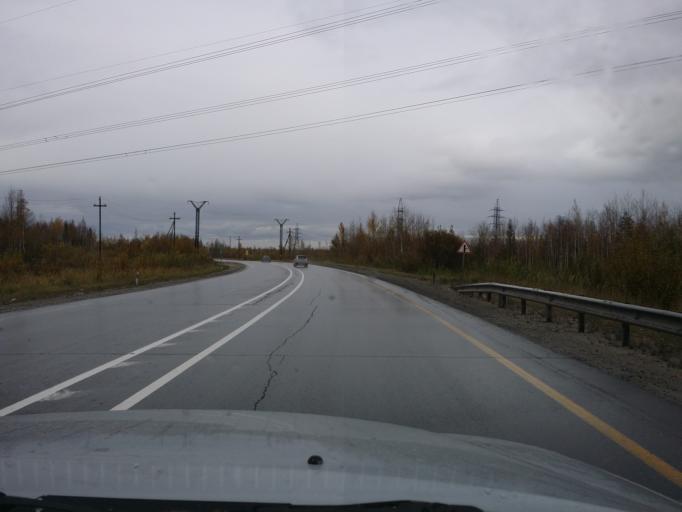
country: RU
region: Khanty-Mansiyskiy Avtonomnyy Okrug
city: Megion
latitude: 61.0820
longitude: 76.1177
